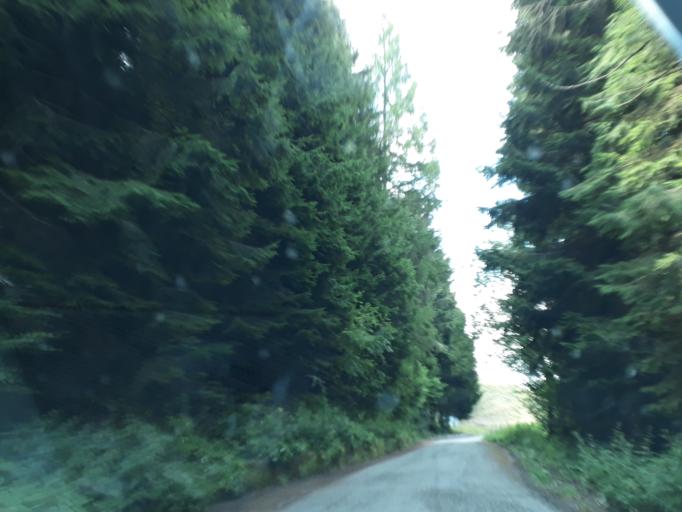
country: IT
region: Trentino-Alto Adige
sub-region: Provincia di Trento
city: Castel Condino
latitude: 45.9312
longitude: 10.5924
